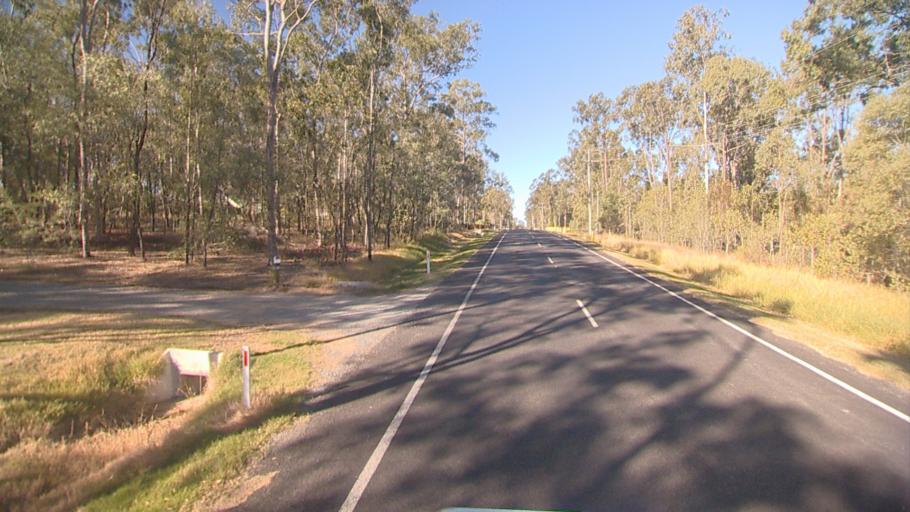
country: AU
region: Queensland
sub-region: Logan
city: North Maclean
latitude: -27.8029
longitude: 153.0270
